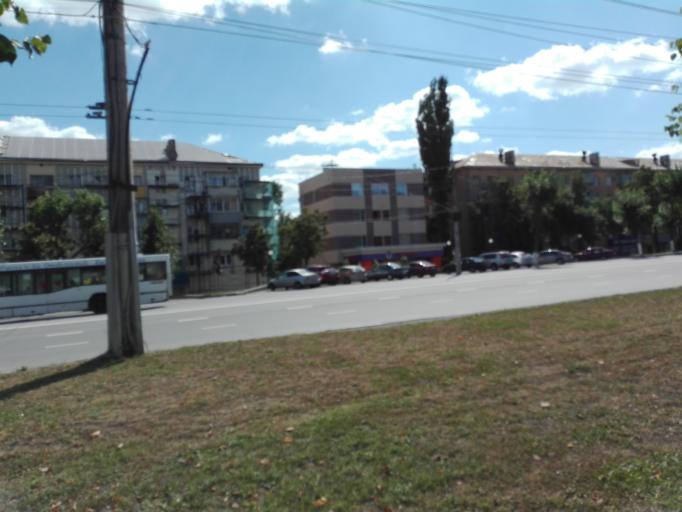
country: RU
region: Lipetsk
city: Lipetsk
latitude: 52.6175
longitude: 39.5943
